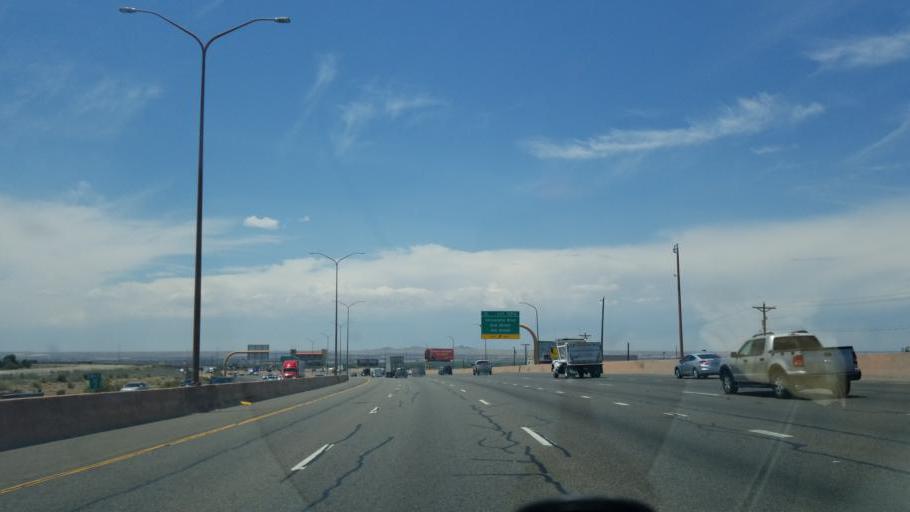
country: US
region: New Mexico
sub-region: Bernalillo County
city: Albuquerque
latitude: 35.1074
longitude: -106.6138
